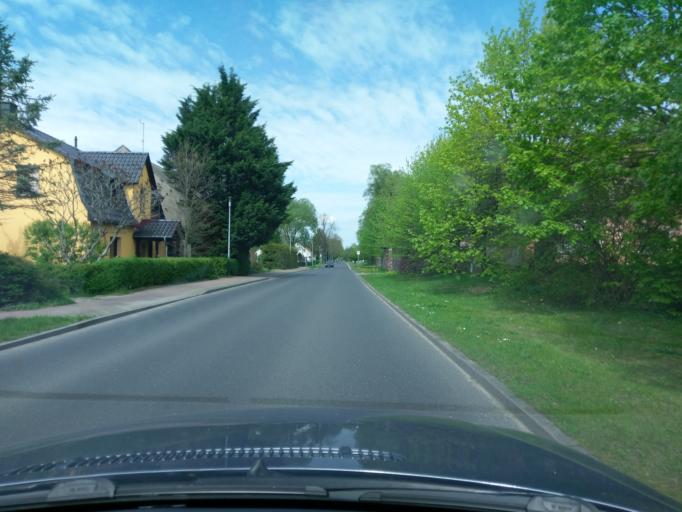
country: DE
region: Brandenburg
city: Werftpfuhl
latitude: 52.7397
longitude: 13.8404
